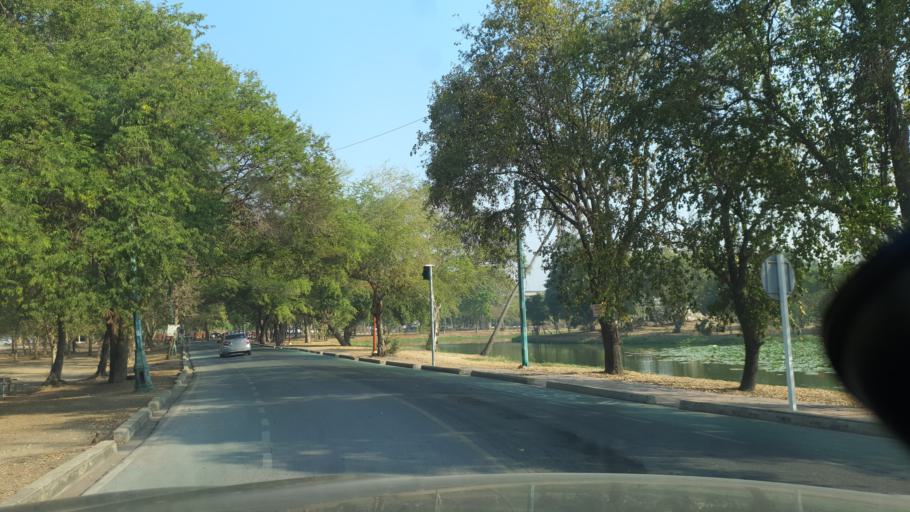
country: TH
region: Phra Nakhon Si Ayutthaya
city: Phra Nakhon Si Ayutthaya
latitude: 14.3554
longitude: 100.5616
